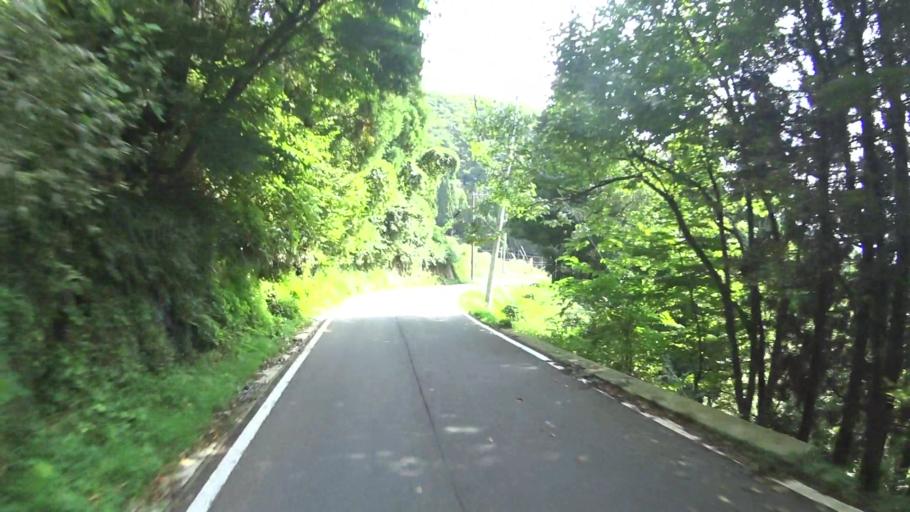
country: JP
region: Kyoto
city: Miyazu
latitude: 35.6404
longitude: 135.1867
